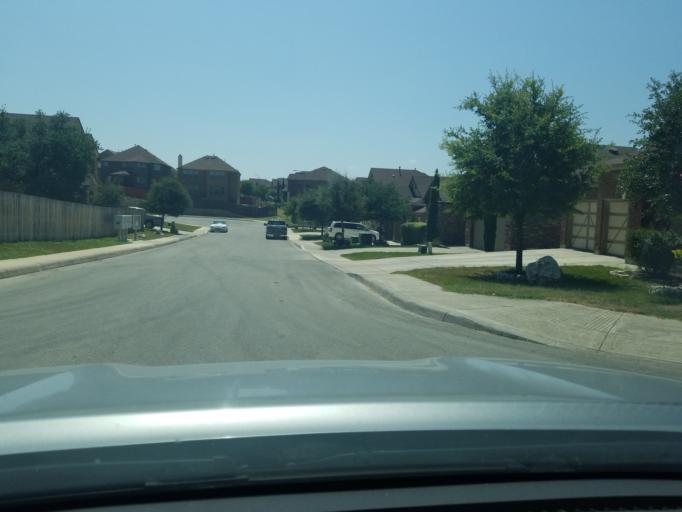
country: US
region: Texas
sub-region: Bexar County
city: Hollywood Park
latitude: 29.6389
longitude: -98.4750
